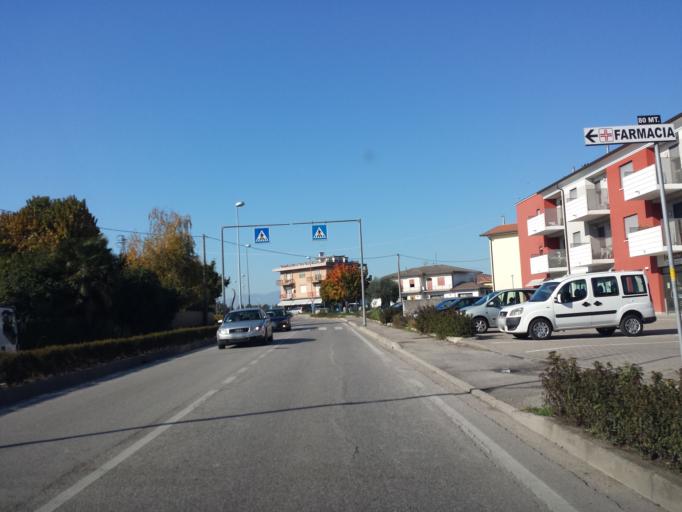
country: IT
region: Veneto
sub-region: Provincia di Vicenza
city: Camisano Vicentino
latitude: 45.5204
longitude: 11.6923
